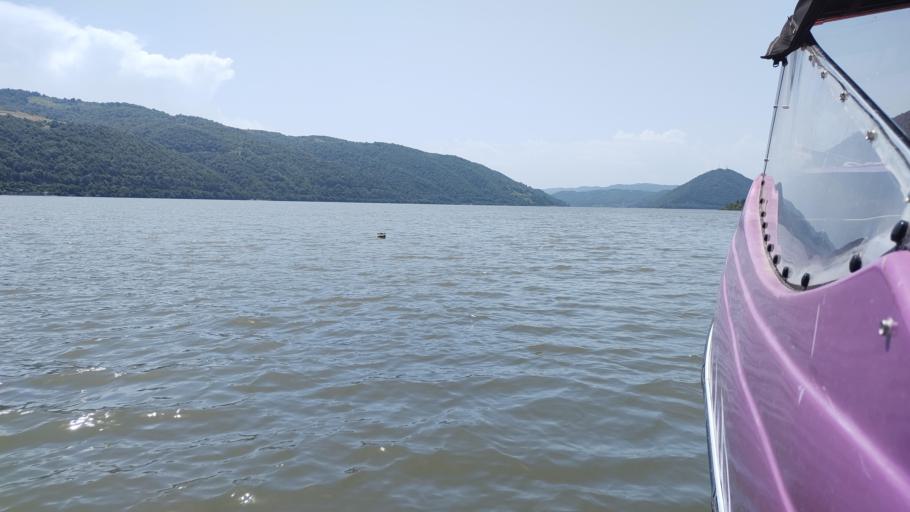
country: RO
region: Mehedinti
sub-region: Comuna Svinita
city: Svinita
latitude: 44.4982
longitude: 22.1889
